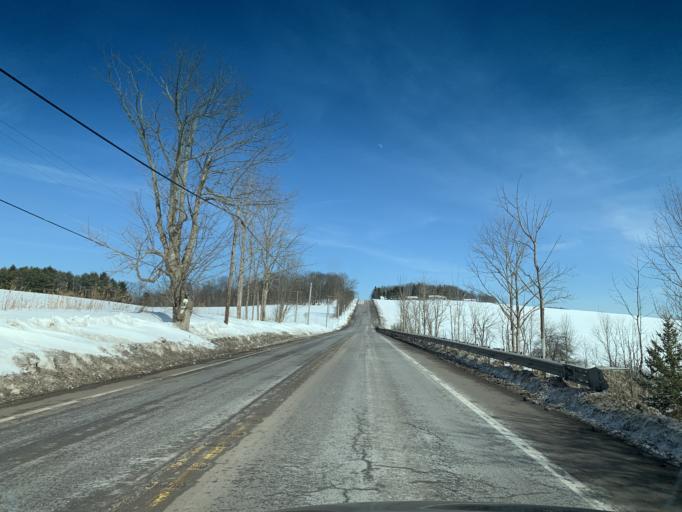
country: US
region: Maryland
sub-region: Allegany County
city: Frostburg
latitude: 39.6844
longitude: -79.0446
